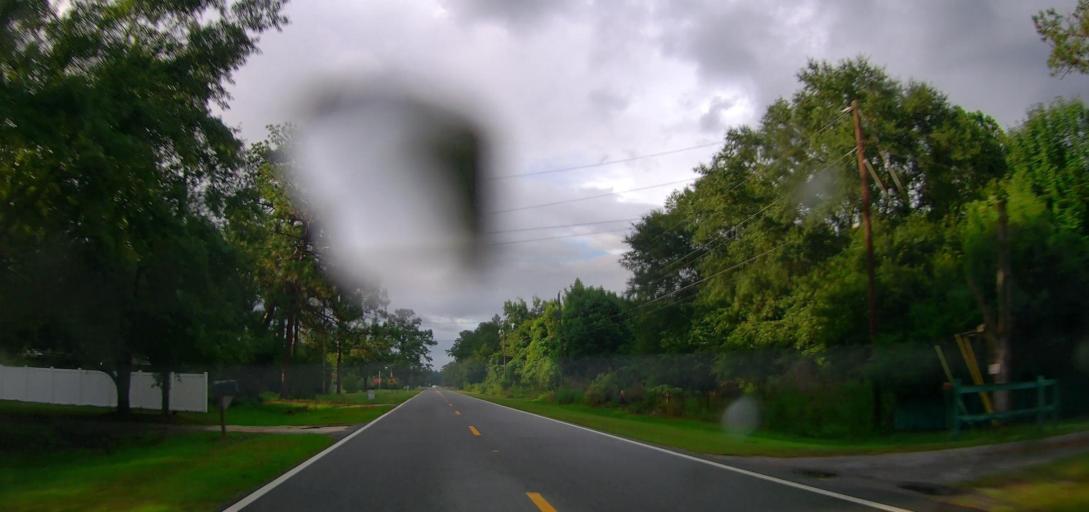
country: US
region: Georgia
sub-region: Ware County
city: Deenwood
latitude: 31.2061
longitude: -82.4014
